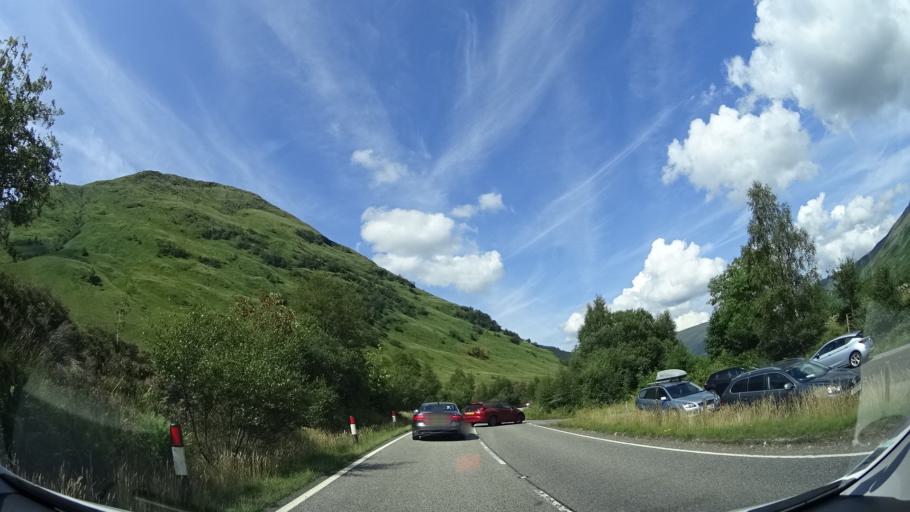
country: GB
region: Scotland
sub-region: Highland
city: Fort William
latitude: 56.6610
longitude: -5.0686
